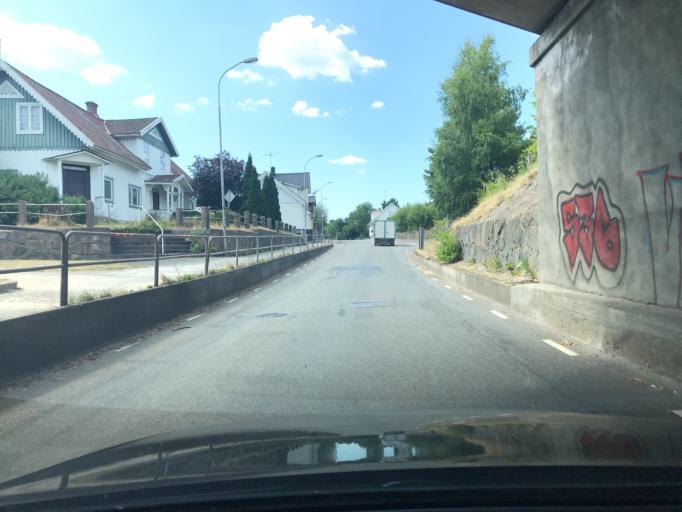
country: SE
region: Skane
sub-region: Hassleholms Kommun
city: Hastveda
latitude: 56.2851
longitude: 13.9334
